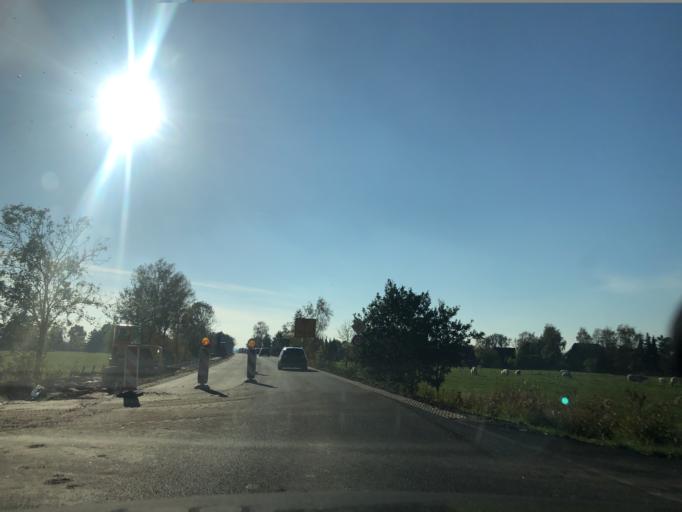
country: DE
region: Lower Saxony
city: Lemwerder
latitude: 53.1497
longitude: 8.5495
